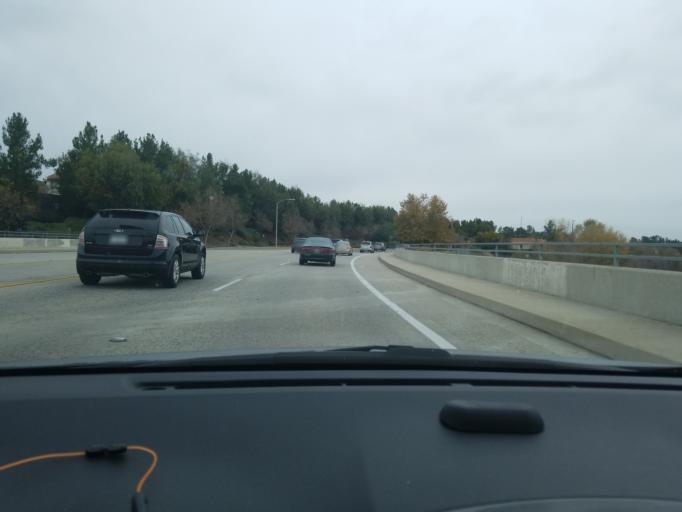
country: US
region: California
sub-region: Riverside County
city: Murrieta Hot Springs
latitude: 33.5333
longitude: -117.1527
